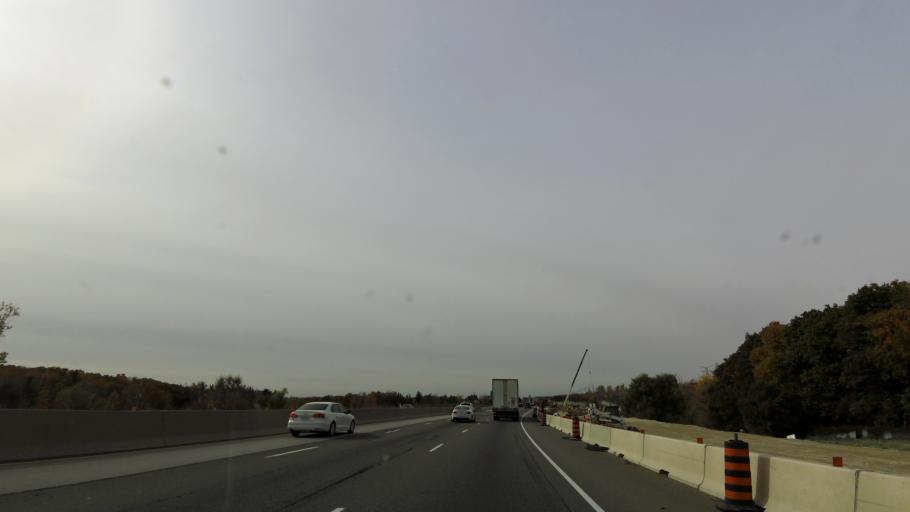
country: CA
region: Ontario
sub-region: Halton
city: Milton
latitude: 43.4962
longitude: -79.9664
